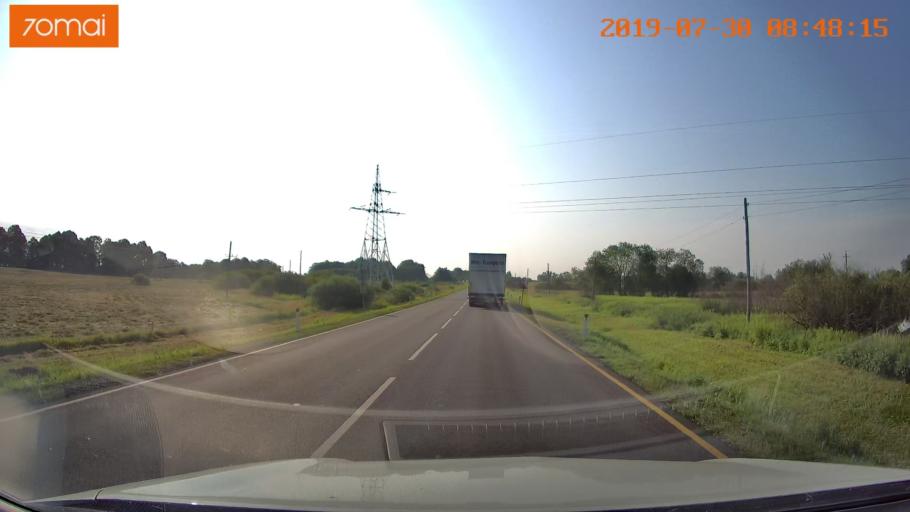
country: RU
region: Kaliningrad
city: Chernyakhovsk
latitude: 54.6188
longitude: 21.9028
